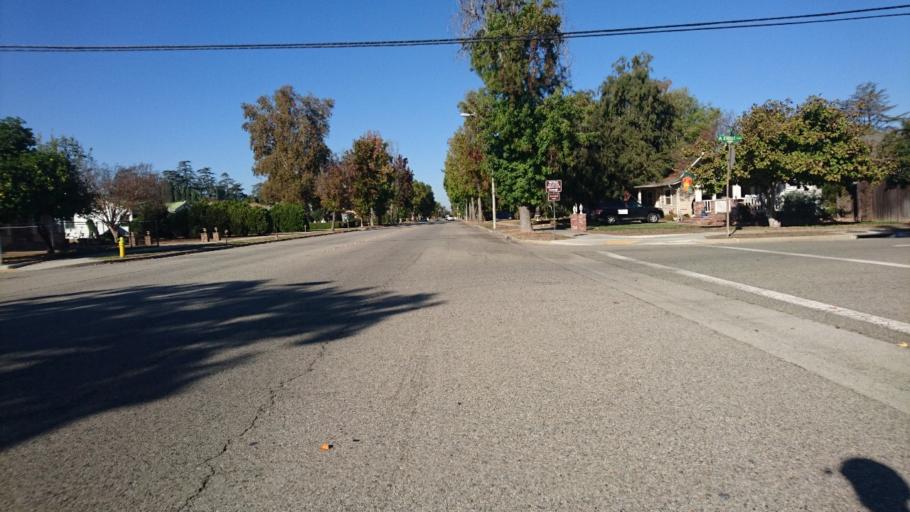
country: US
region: California
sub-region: Los Angeles County
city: La Verne
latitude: 34.1031
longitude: -117.7756
